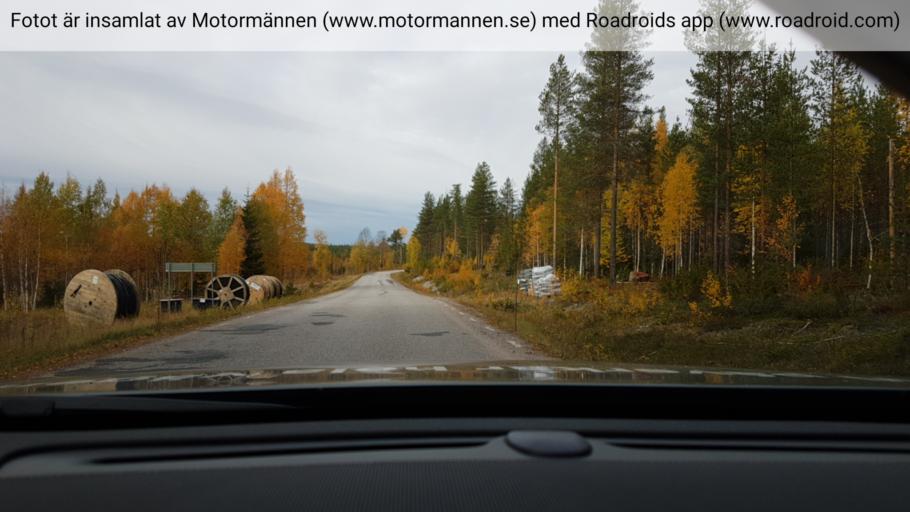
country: SE
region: Norrbotten
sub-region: Overkalix Kommun
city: OEverkalix
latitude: 66.2558
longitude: 23.1191
